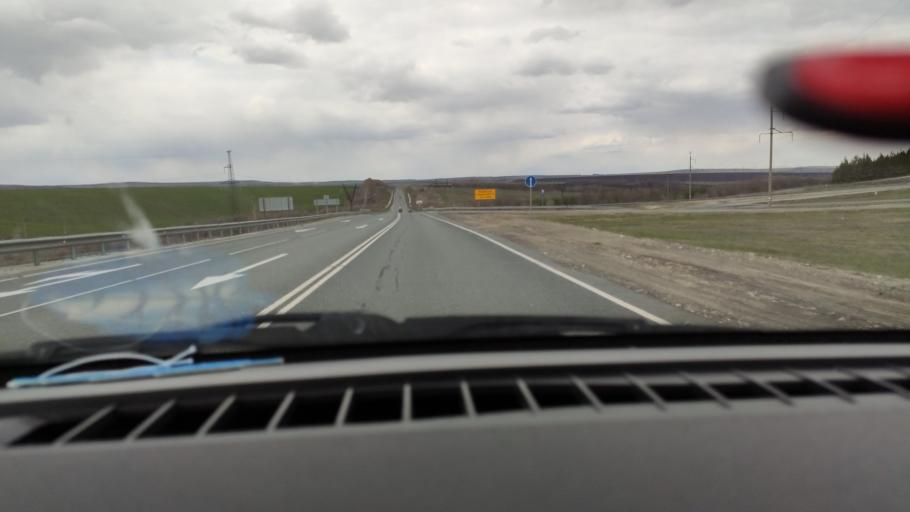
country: RU
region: Saratov
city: Shikhany
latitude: 52.1152
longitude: 47.2979
